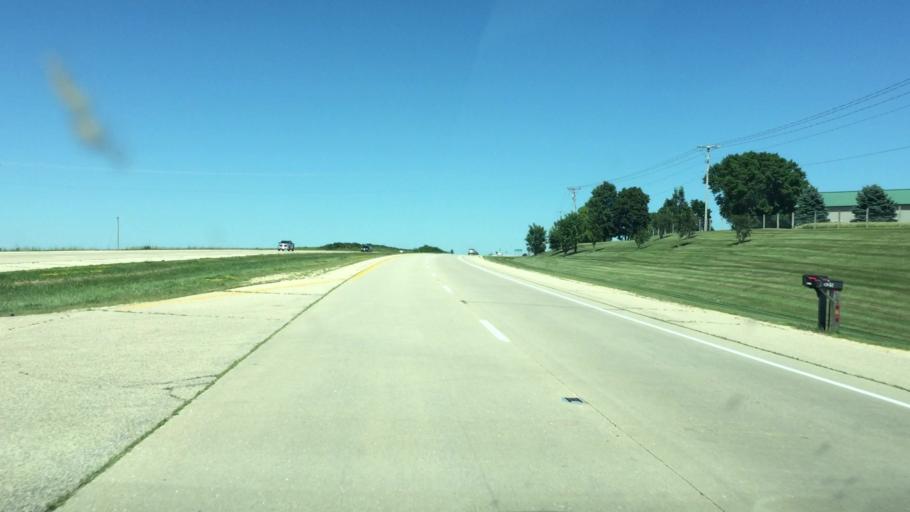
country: US
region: Wisconsin
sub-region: Iowa County
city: Mineral Point
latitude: 42.8322
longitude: -90.2309
